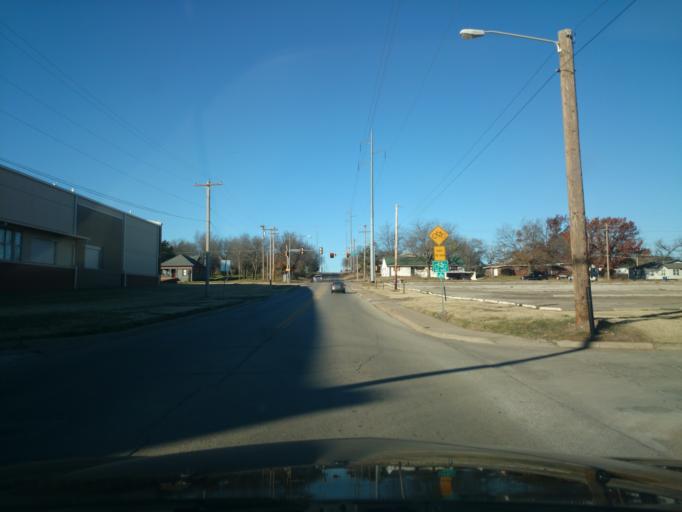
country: US
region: Oklahoma
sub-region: Payne County
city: Stillwater
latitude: 36.1305
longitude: -97.0682
